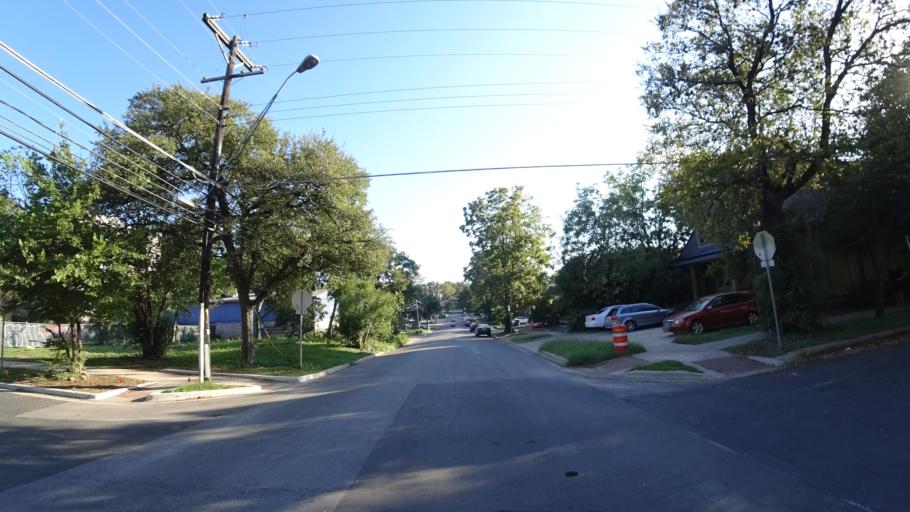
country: US
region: Texas
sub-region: Travis County
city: Austin
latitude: 30.2855
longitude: -97.7481
